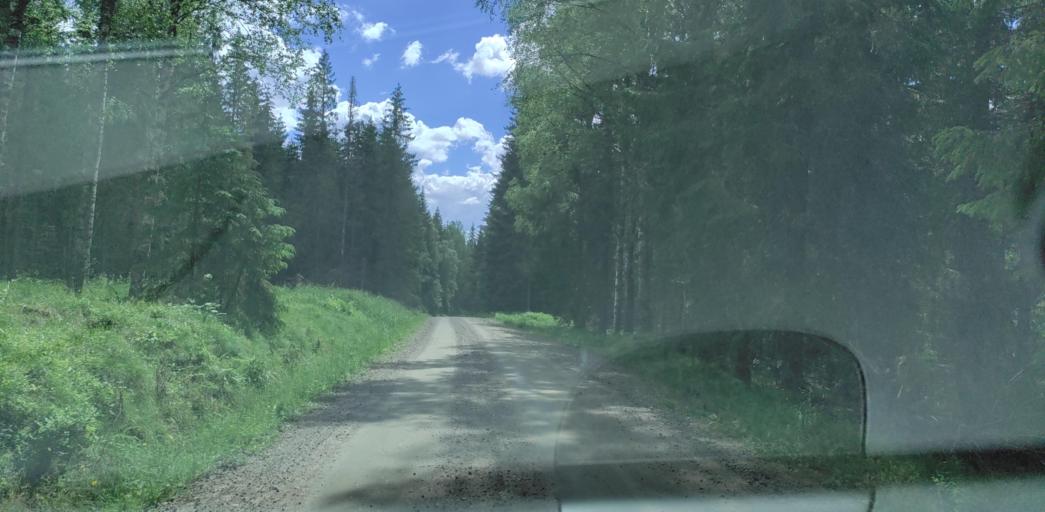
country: SE
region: Vaermland
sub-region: Hagfors Kommun
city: Ekshaerad
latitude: 60.0656
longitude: 13.3070
